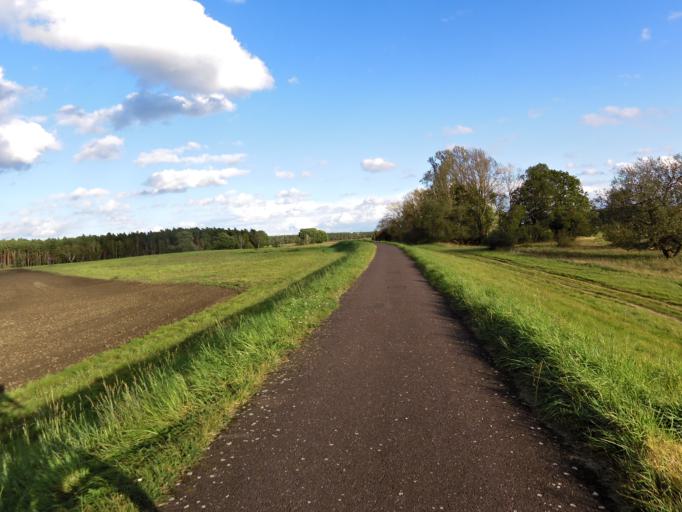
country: DE
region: Saxony-Anhalt
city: Schonebeck
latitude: 52.0725
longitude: 11.6937
